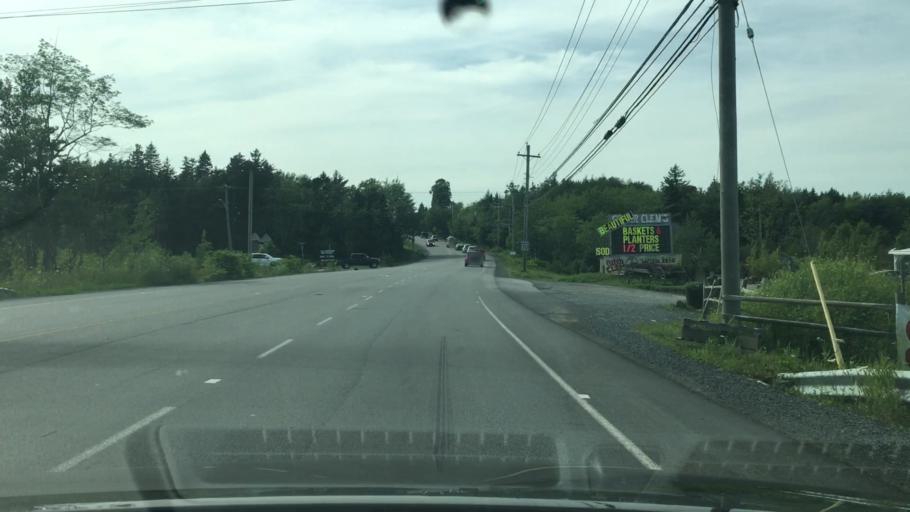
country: CA
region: Nova Scotia
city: Dartmouth
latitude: 44.7287
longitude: -63.7493
